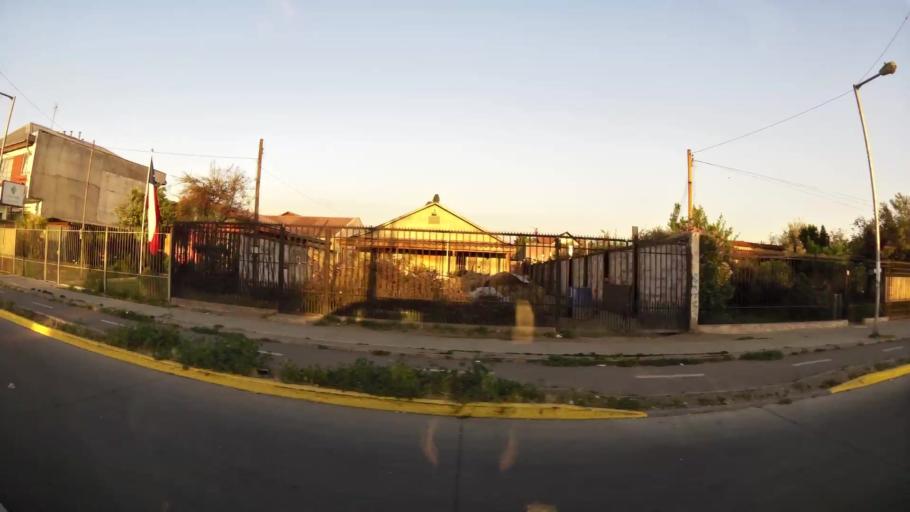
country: CL
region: Santiago Metropolitan
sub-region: Provincia de Maipo
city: San Bernardo
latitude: -33.5626
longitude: -70.6711
